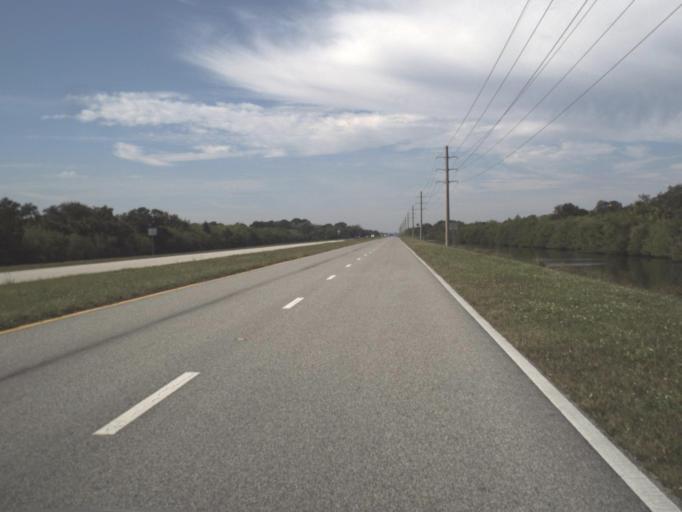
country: US
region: Florida
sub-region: Brevard County
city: Merritt Island
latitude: 28.5264
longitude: -80.7049
